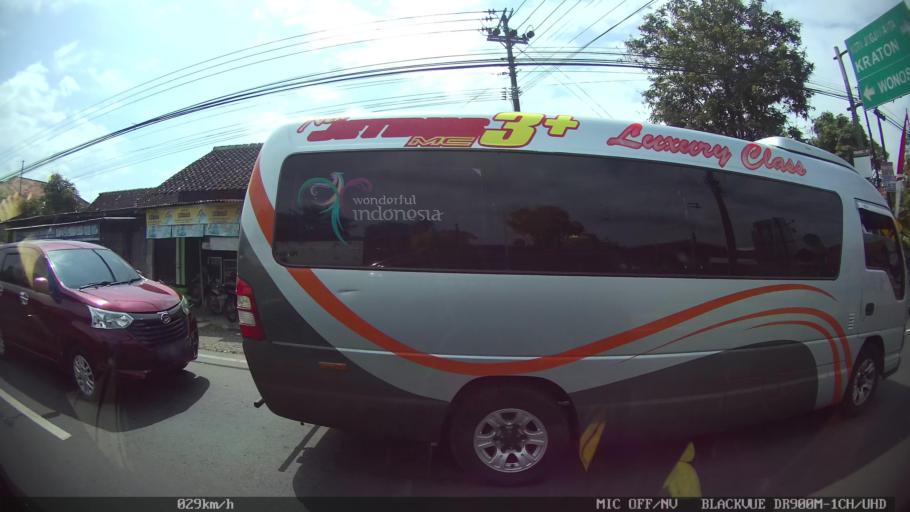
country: ID
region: Daerah Istimewa Yogyakarta
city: Depok
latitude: -7.8368
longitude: 110.4766
